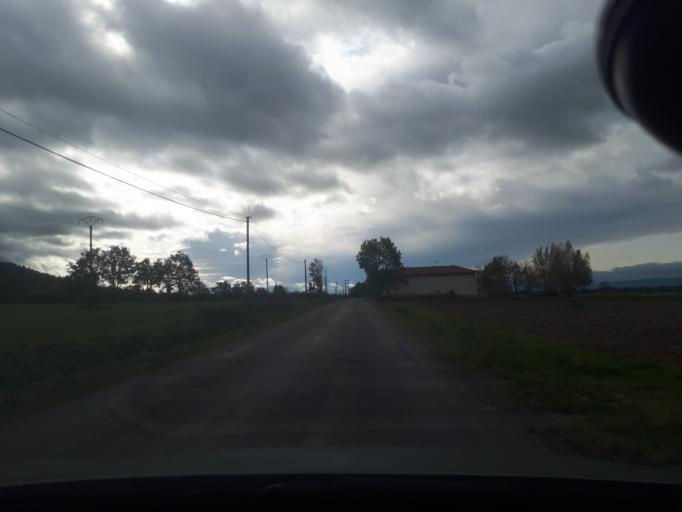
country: FR
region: Rhone-Alpes
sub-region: Departement de la Loire
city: Bellegarde-en-Forez
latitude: 45.6665
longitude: 4.2928
